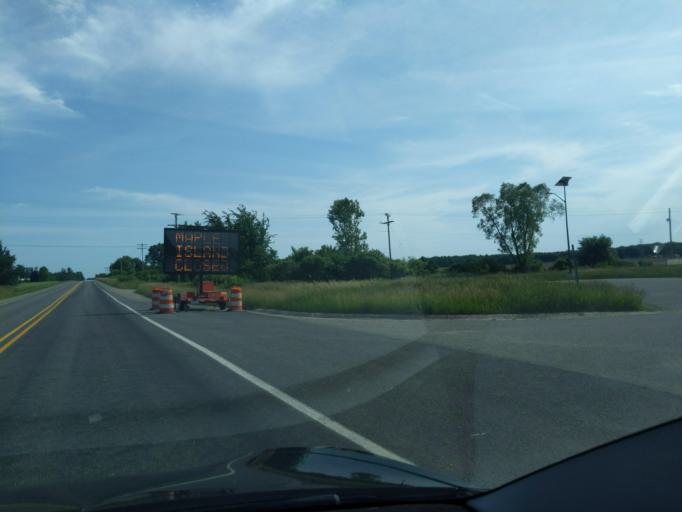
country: US
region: Michigan
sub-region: Newaygo County
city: Fremont
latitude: 43.4248
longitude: -86.0392
